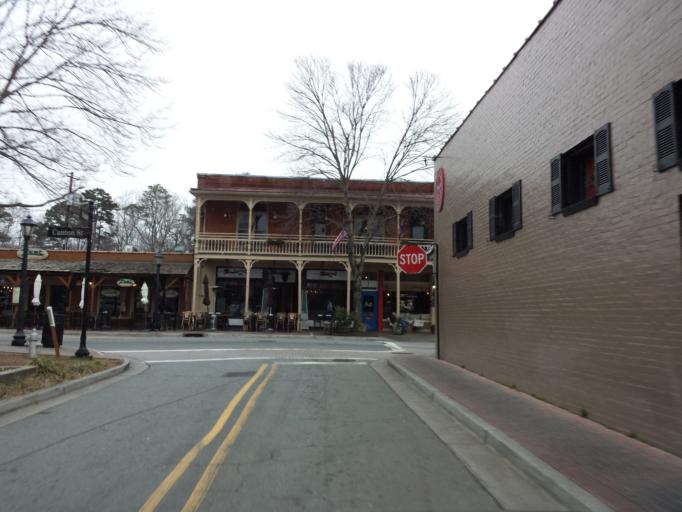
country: US
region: Georgia
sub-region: Fulton County
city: Roswell
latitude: 34.0247
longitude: -84.3617
